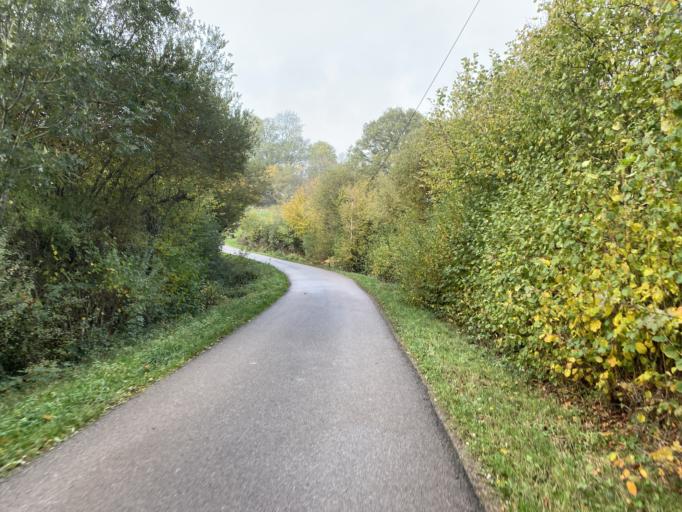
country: FR
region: Bourgogne
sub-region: Departement de la Cote-d'Or
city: Saulieu
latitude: 47.2711
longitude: 4.1775
